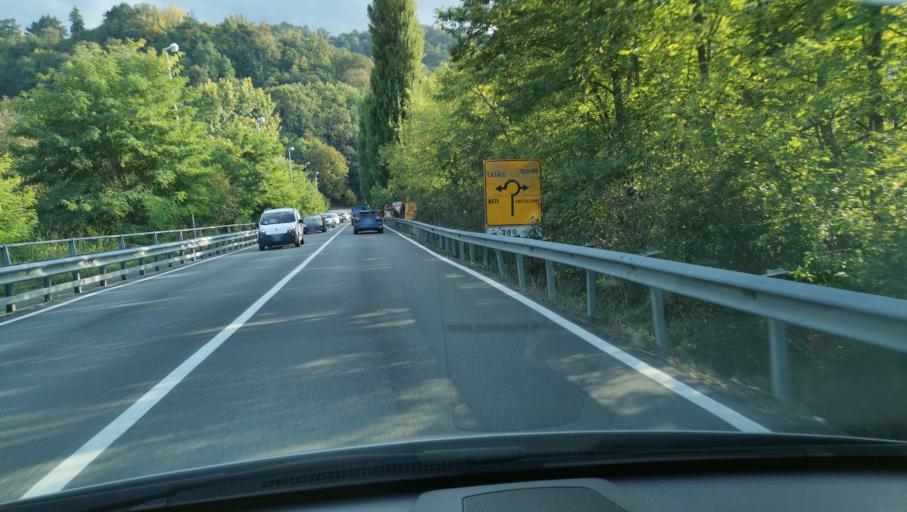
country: IT
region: Piedmont
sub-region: Provincia di Torino
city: Chivasso
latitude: 45.1793
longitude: 7.8905
